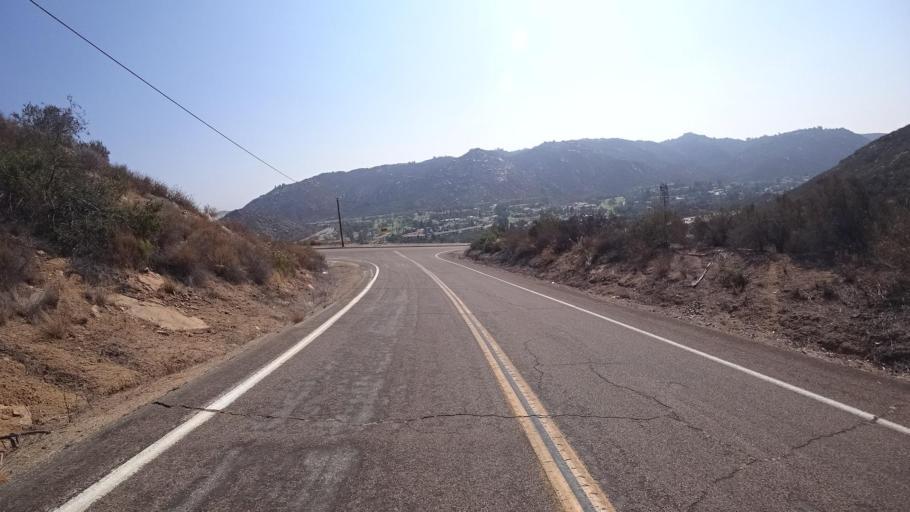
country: US
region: California
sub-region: San Diego County
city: Hidden Meadows
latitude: 33.2337
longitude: -117.1512
